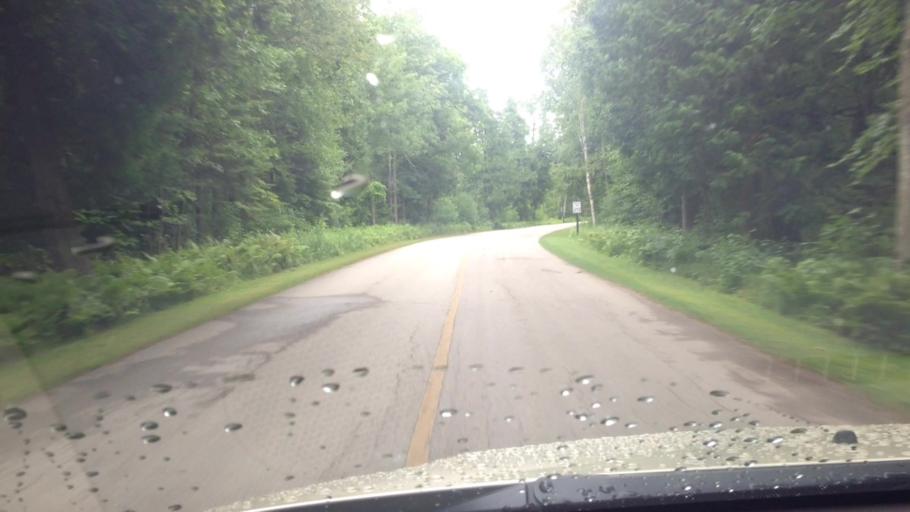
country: US
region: Michigan
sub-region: Menominee County
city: Menominee
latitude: 45.3896
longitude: -87.3685
